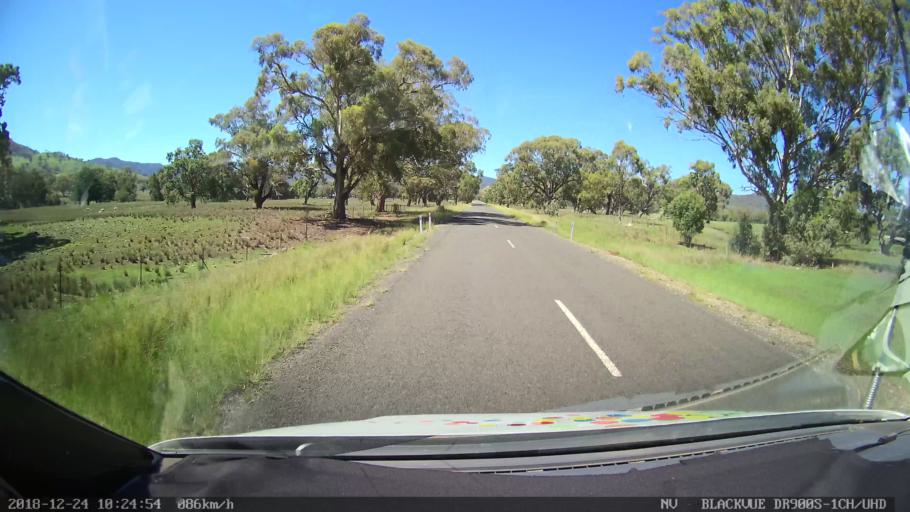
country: AU
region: New South Wales
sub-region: Liverpool Plains
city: Quirindi
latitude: -31.7922
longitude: 150.5308
